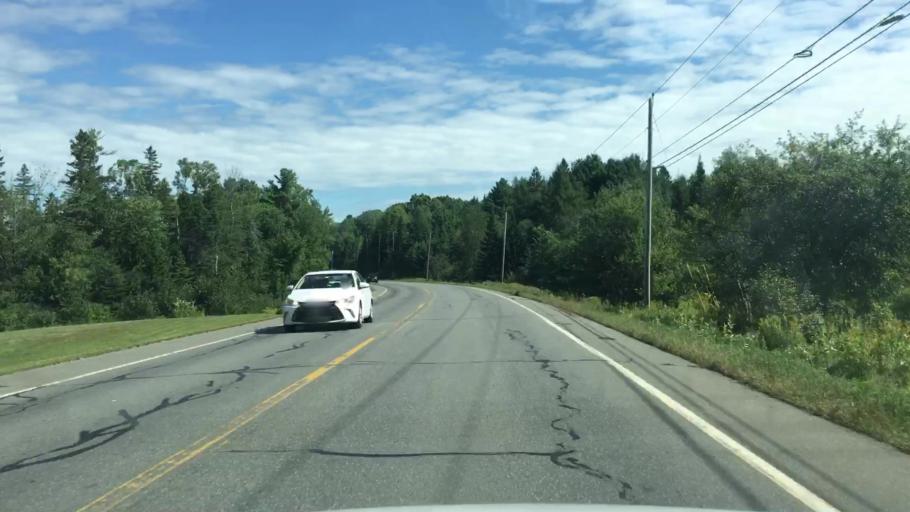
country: US
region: Maine
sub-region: Penobscot County
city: Garland
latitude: 45.0915
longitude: -69.2149
